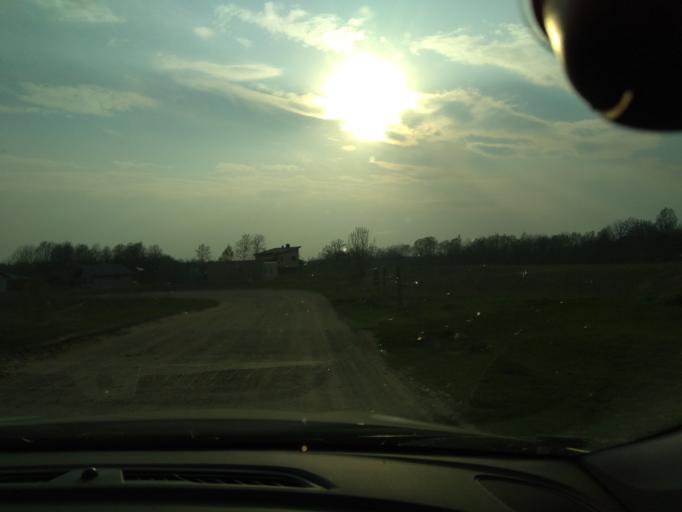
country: LT
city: Baltoji Voke
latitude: 54.5949
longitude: 25.1608
